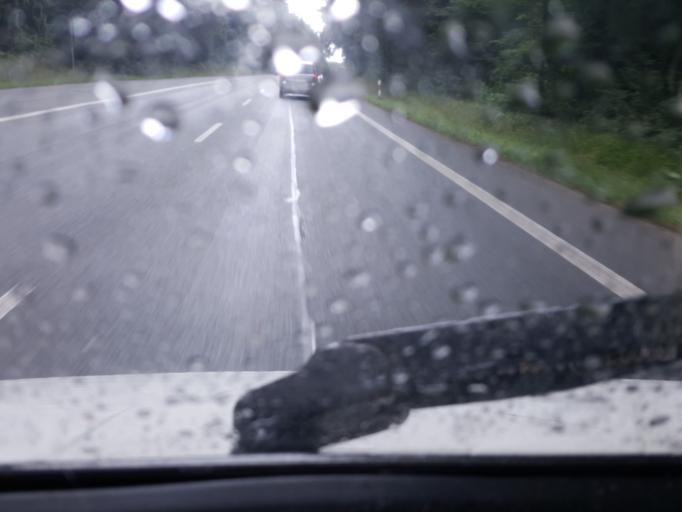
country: DE
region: North Rhine-Westphalia
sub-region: Regierungsbezirk Detmold
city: Petershagen
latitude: 52.3519
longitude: 8.9507
